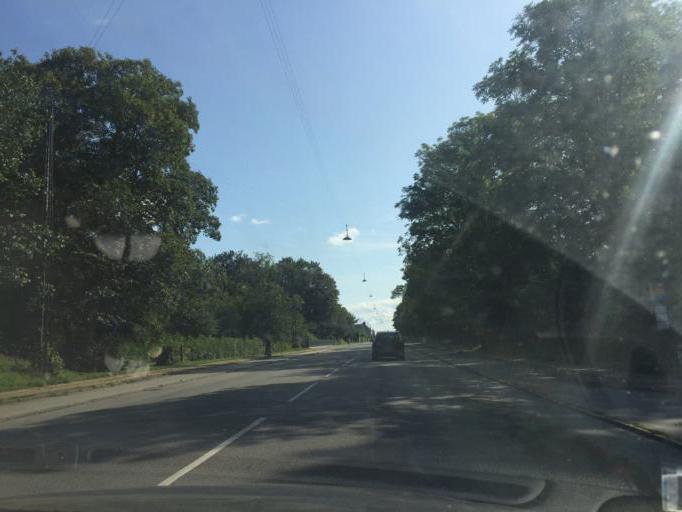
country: DK
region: Capital Region
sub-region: Herlev Kommune
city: Herlev
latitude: 55.7178
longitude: 12.4702
